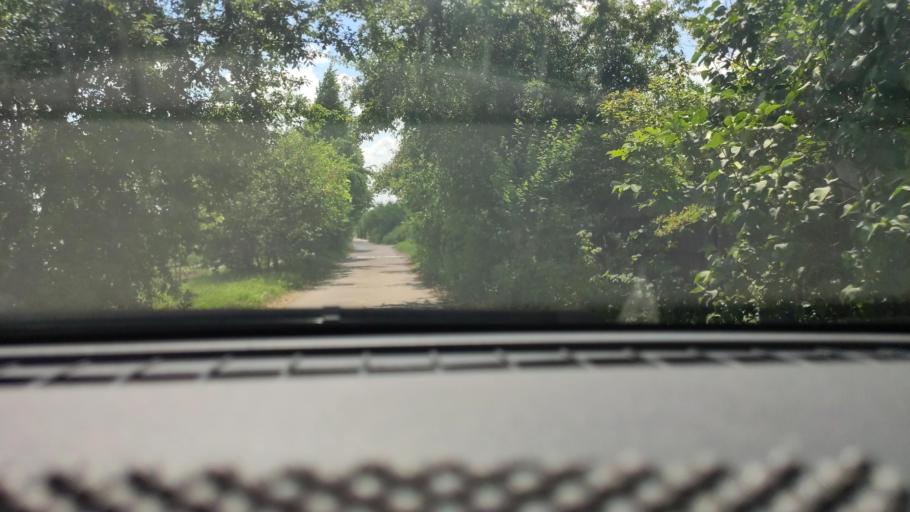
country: RU
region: Voronezj
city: Ramon'
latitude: 51.9100
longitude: 39.1772
